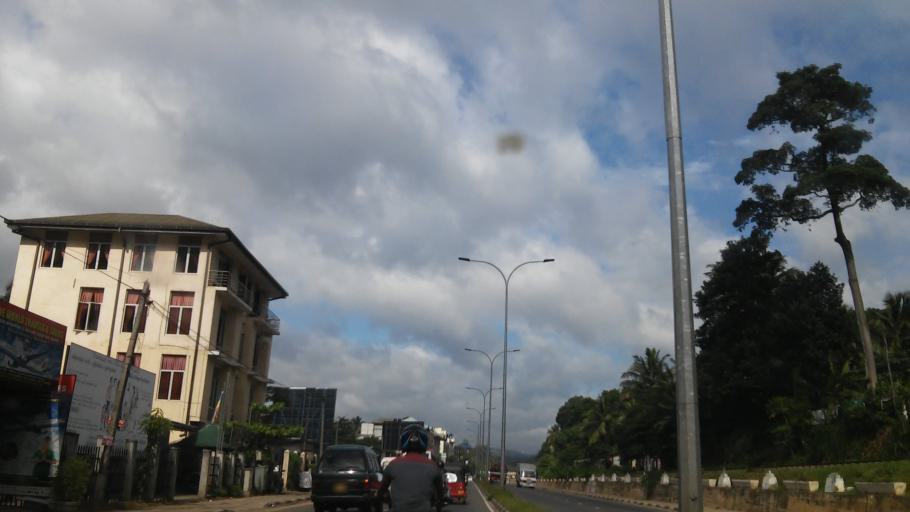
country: LK
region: Central
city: Kandy
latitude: 7.2758
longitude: 80.6152
